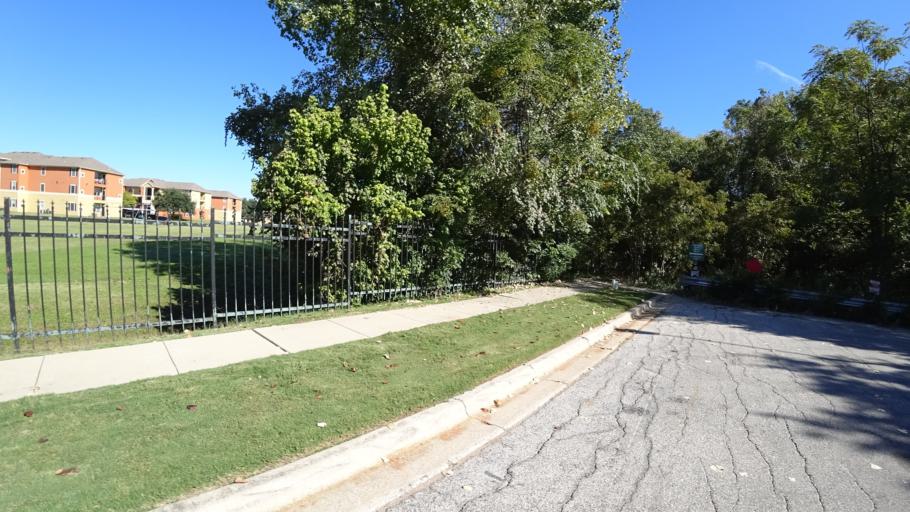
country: US
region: Texas
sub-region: Travis County
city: Austin
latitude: 30.2375
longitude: -97.7156
